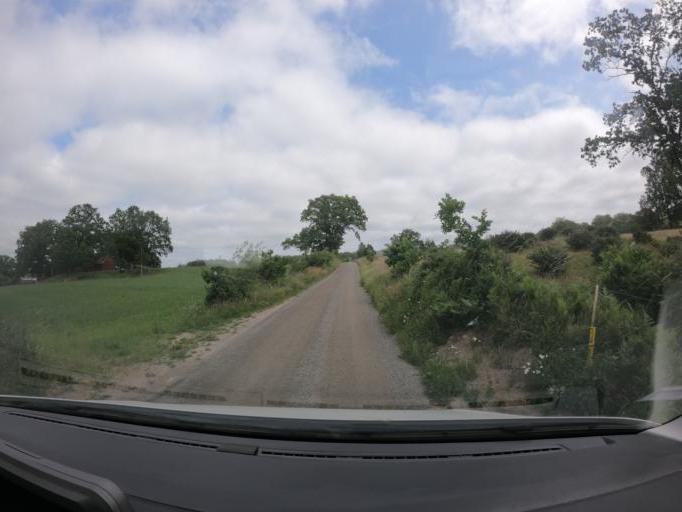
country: SE
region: Skane
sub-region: Hassleholms Kommun
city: Sosdala
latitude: 56.0653
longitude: 13.6638
